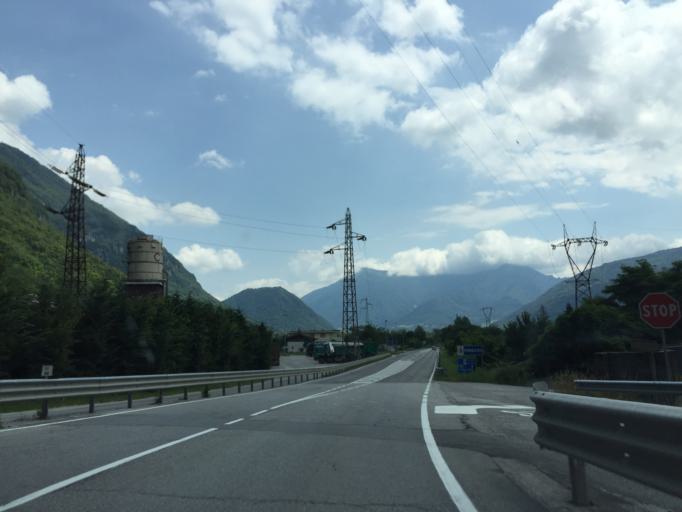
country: IT
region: Veneto
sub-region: Provincia di Belluno
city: Fonzaso
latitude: 46.0217
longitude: 11.7782
